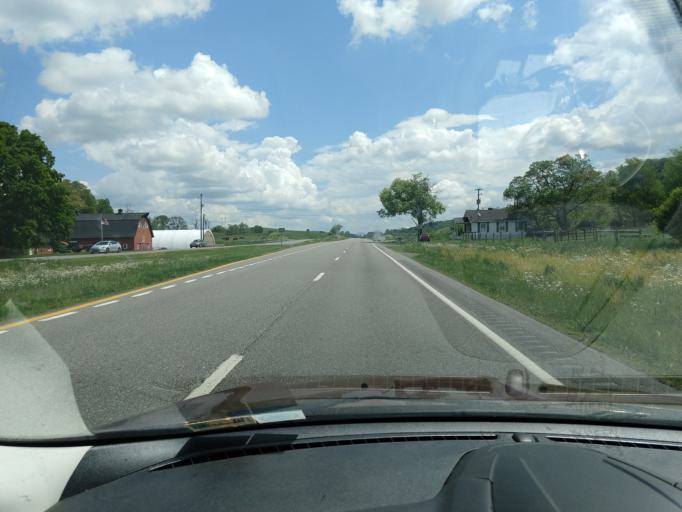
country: US
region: Virginia
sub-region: Russell County
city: Honaker
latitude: 36.9681
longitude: -81.9109
